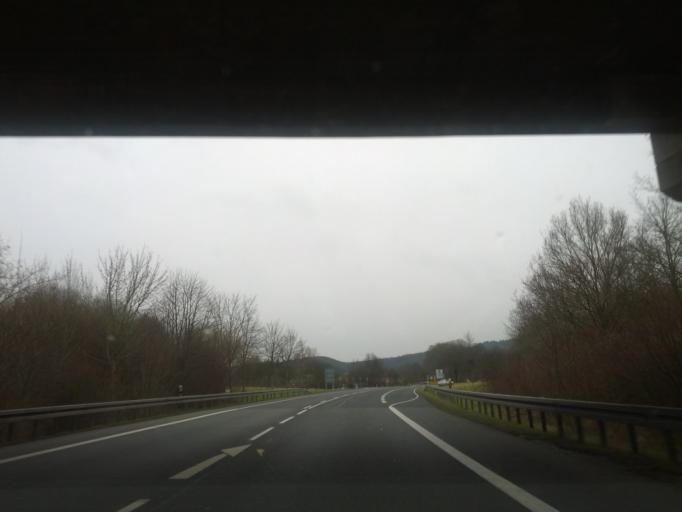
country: DE
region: Hesse
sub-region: Regierungsbezirk Kassel
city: Bad Sooden-Allendorf
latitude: 51.2734
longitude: 9.9668
